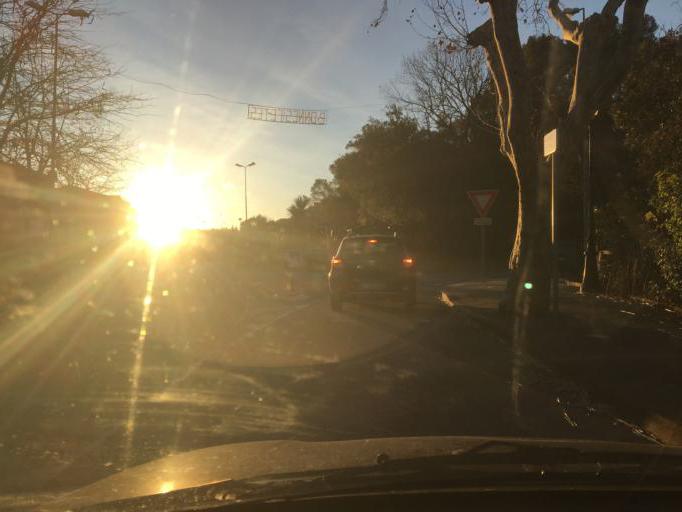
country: FR
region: Provence-Alpes-Cote d'Azur
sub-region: Departement du Var
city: Taradeau
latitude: 43.4523
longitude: 6.4293
